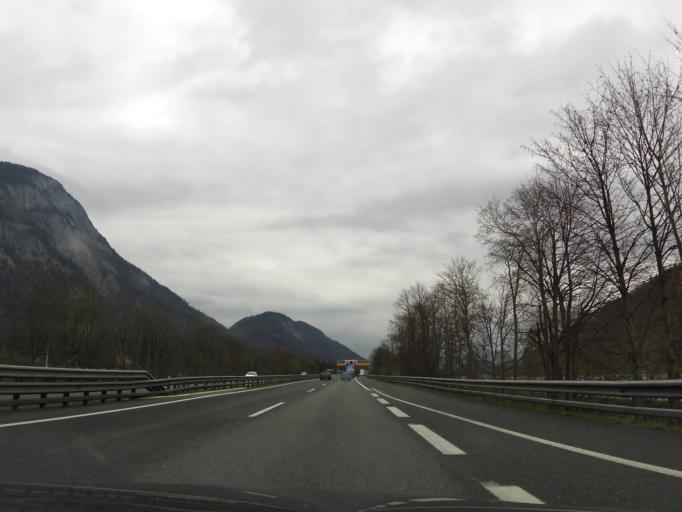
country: AT
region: Tyrol
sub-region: Politischer Bezirk Kufstein
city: Schwoich
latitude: 47.5472
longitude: 12.1189
